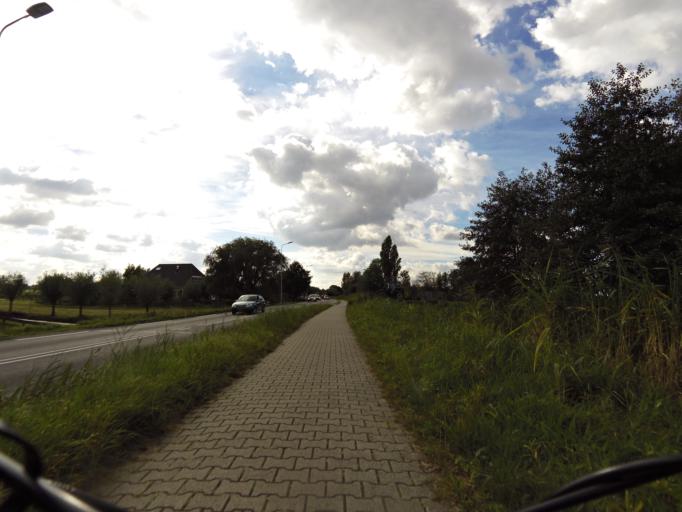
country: NL
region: South Holland
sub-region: Gemeente Voorschoten
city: Voorschoten
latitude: 52.1026
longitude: 4.4834
